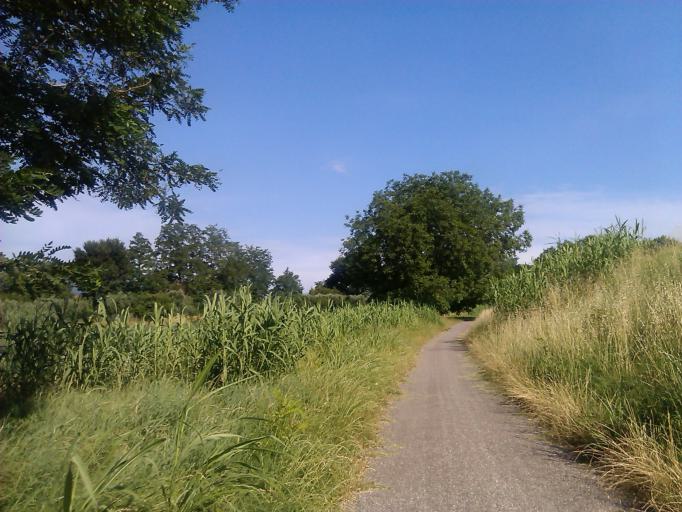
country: IT
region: Tuscany
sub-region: Province of Florence
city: Campi Bisenzio
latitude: 43.8605
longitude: 11.1235
